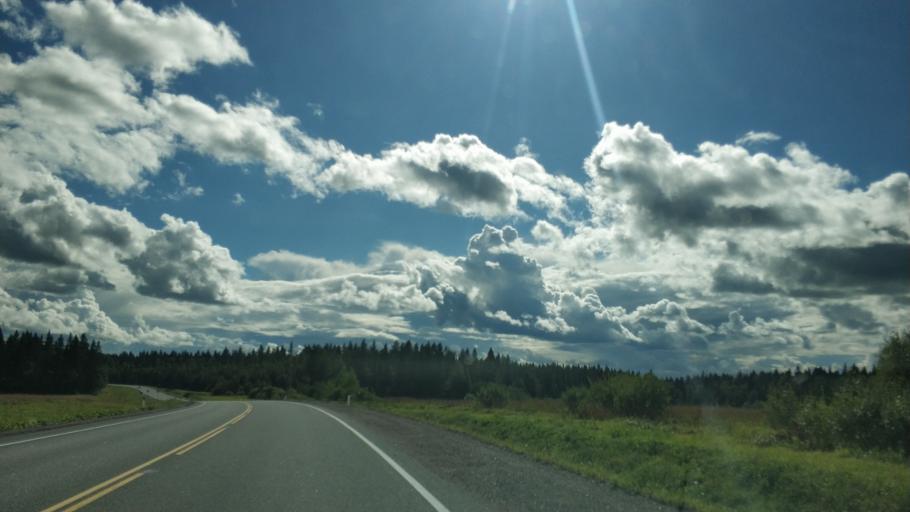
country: RU
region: Republic of Karelia
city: Ruskeala
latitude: 61.8825
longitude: 30.6434
